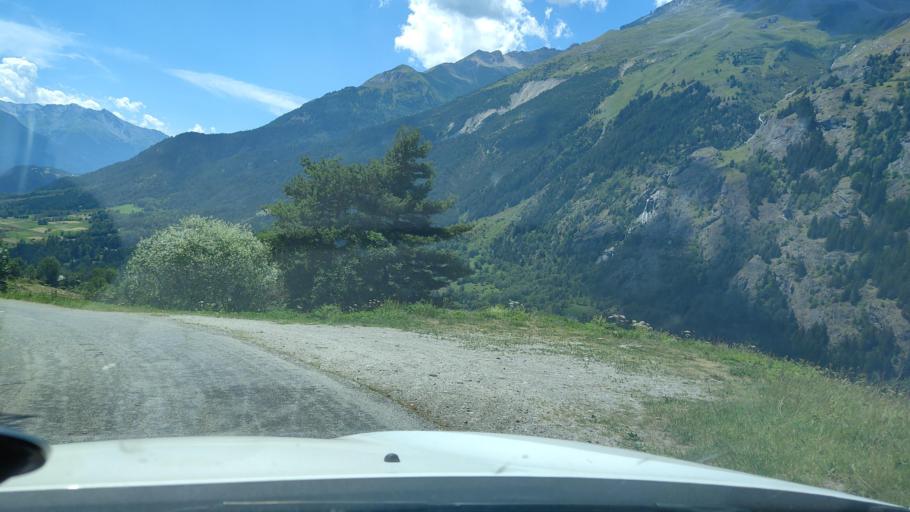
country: FR
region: Rhone-Alpes
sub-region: Departement de la Savoie
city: Modane
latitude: 45.2919
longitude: 6.8203
